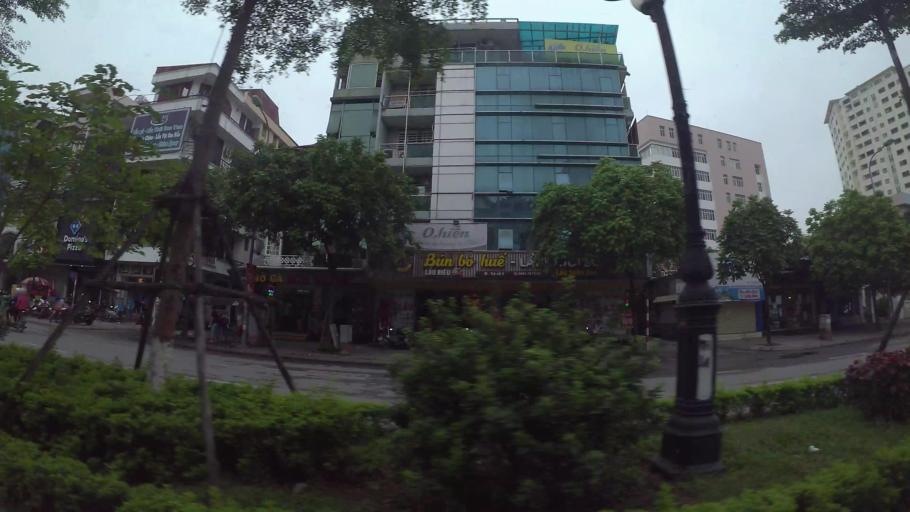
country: VN
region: Ha Noi
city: Cau Giay
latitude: 21.0150
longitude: 105.7951
